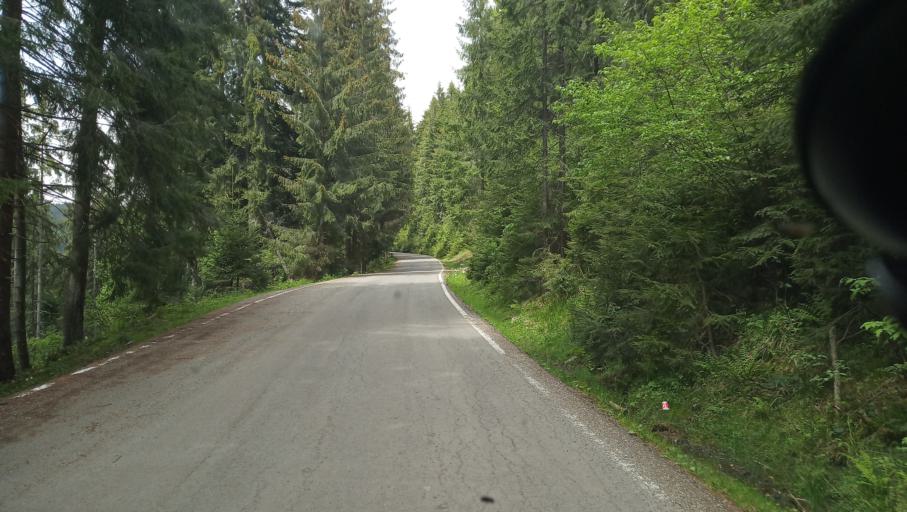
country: RO
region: Alba
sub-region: Comuna Horea
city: Horea
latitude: 46.5202
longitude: 22.8888
